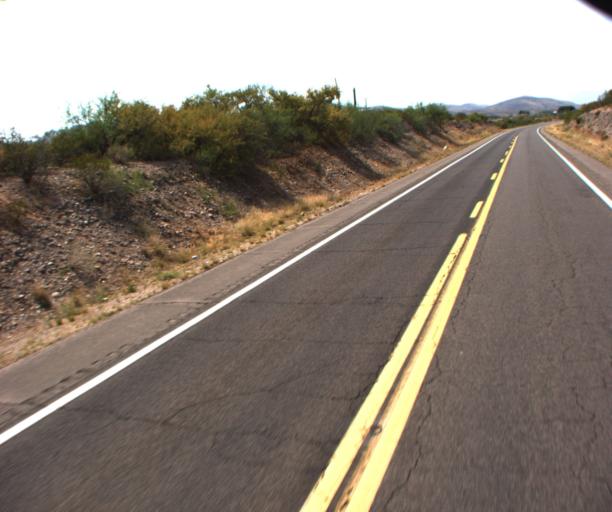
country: US
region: Arizona
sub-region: Greenlee County
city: Clifton
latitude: 32.8138
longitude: -109.1699
